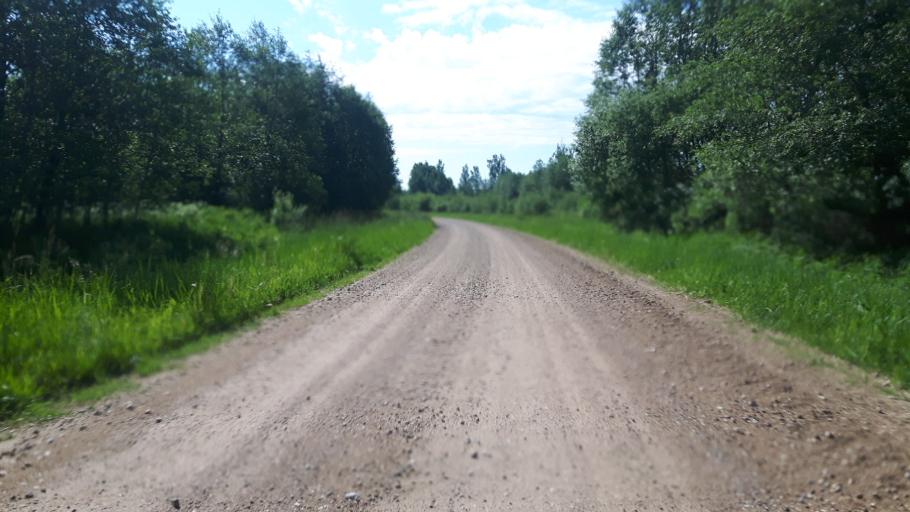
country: EE
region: Paernumaa
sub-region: Vaendra vald (alev)
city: Vandra
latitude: 58.6871
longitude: 25.0328
